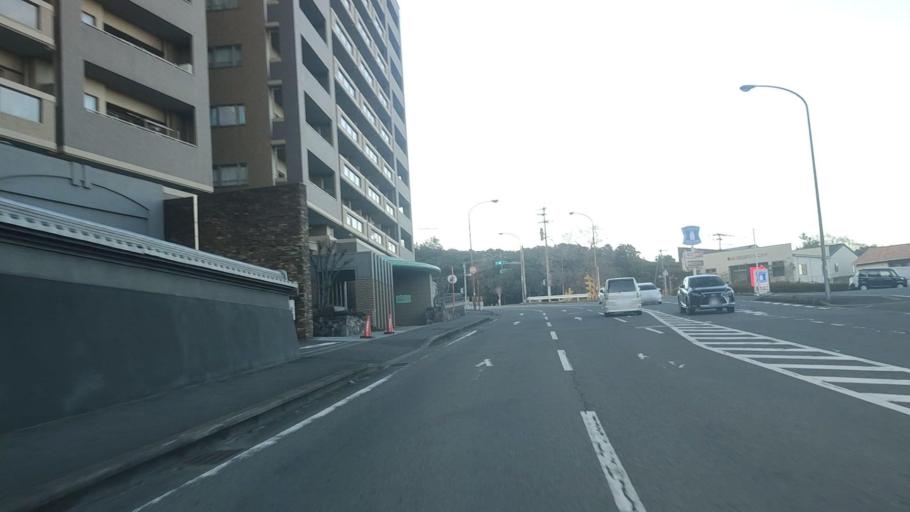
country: JP
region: Oita
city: Beppu
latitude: 33.2839
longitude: 131.4806
